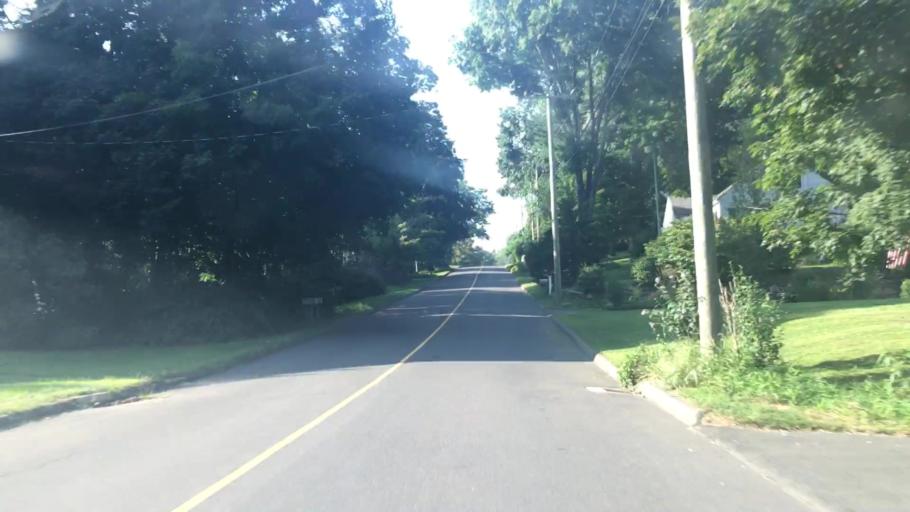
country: US
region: Connecticut
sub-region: Middlesex County
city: Chester Center
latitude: 41.4017
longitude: -72.4601
